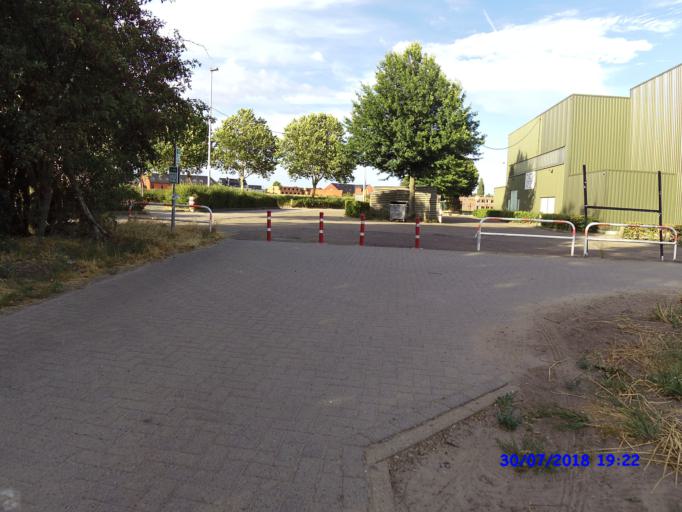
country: BE
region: Flanders
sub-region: Provincie Antwerpen
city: Geel
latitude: 51.1622
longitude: 4.9573
